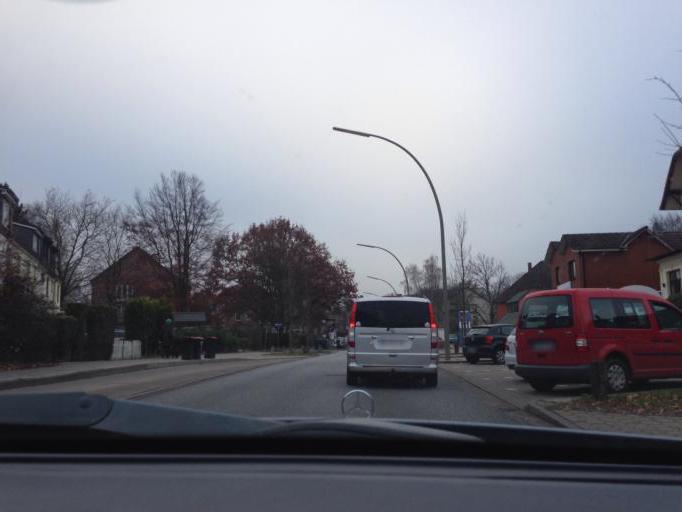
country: DE
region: Hamburg
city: Farmsen-Berne
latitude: 53.5955
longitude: 10.1152
